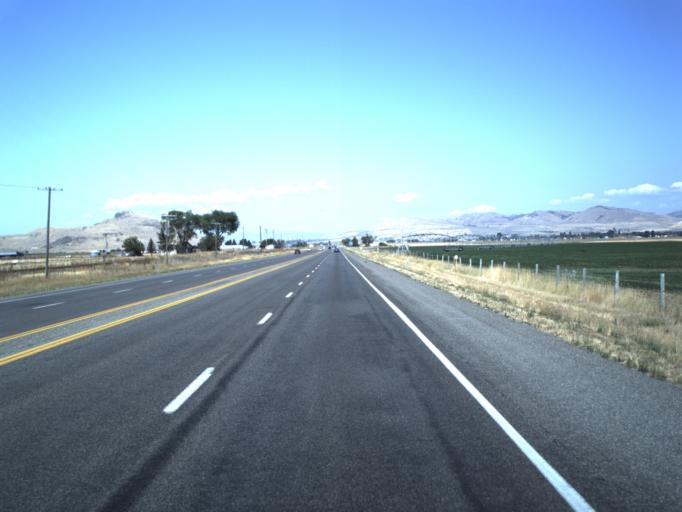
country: US
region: Utah
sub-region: Cache County
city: Lewiston
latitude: 41.9833
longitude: -111.8127
